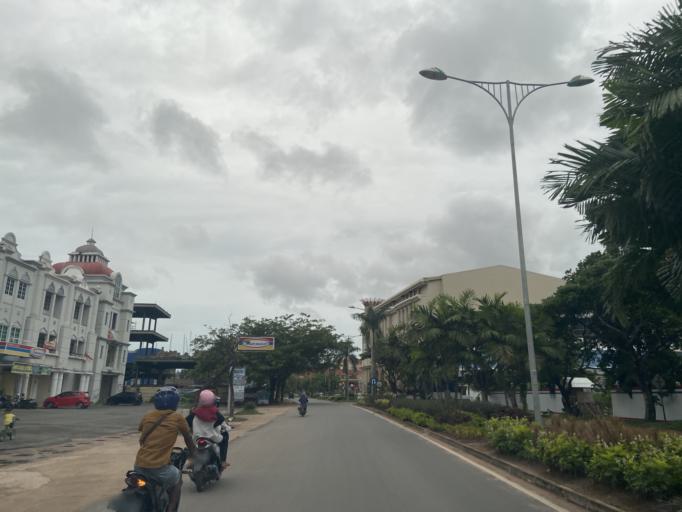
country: SG
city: Singapore
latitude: 1.1333
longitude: 104.0477
